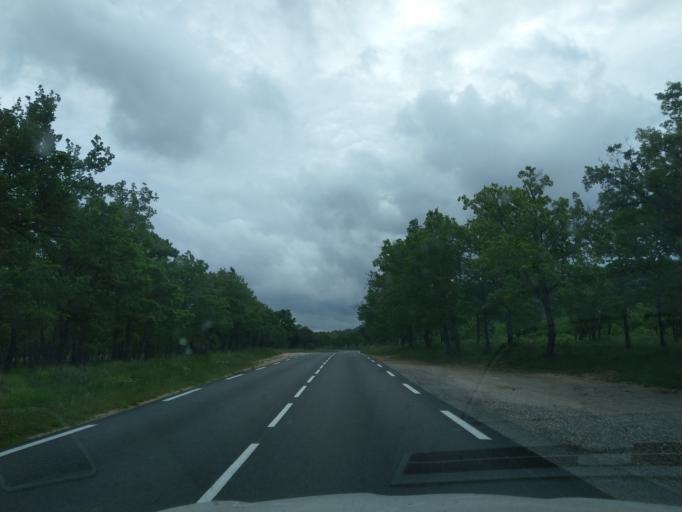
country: FR
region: Provence-Alpes-Cote d'Azur
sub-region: Departement du Var
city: Signes
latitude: 43.2770
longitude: 5.8089
